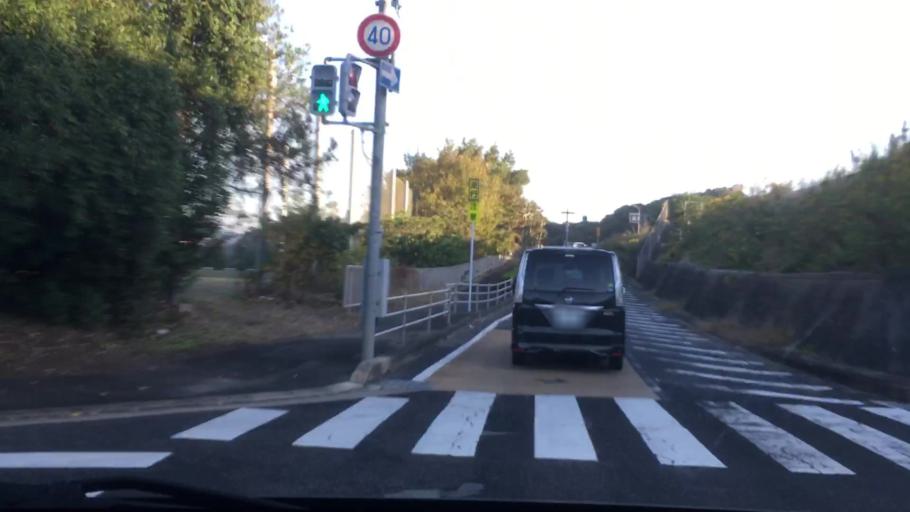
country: JP
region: Nagasaki
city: Sasebo
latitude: 33.1453
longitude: 129.7790
